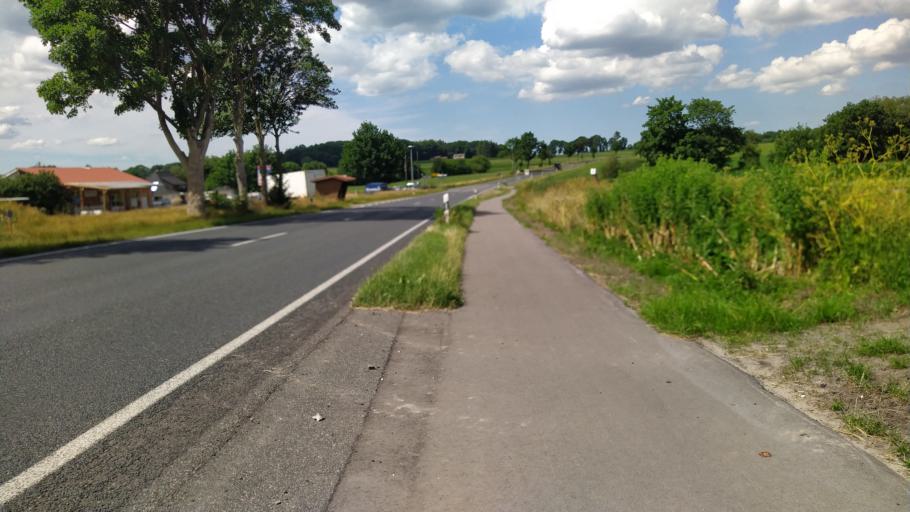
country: DE
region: Lower Saxony
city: Armstorf
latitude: 53.5983
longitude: 9.0813
